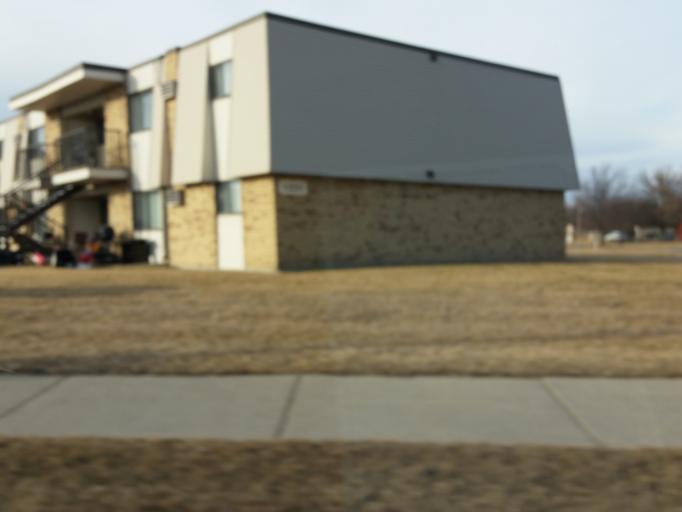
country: US
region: North Dakota
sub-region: Cass County
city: West Fargo
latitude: 46.8625
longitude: -96.8982
